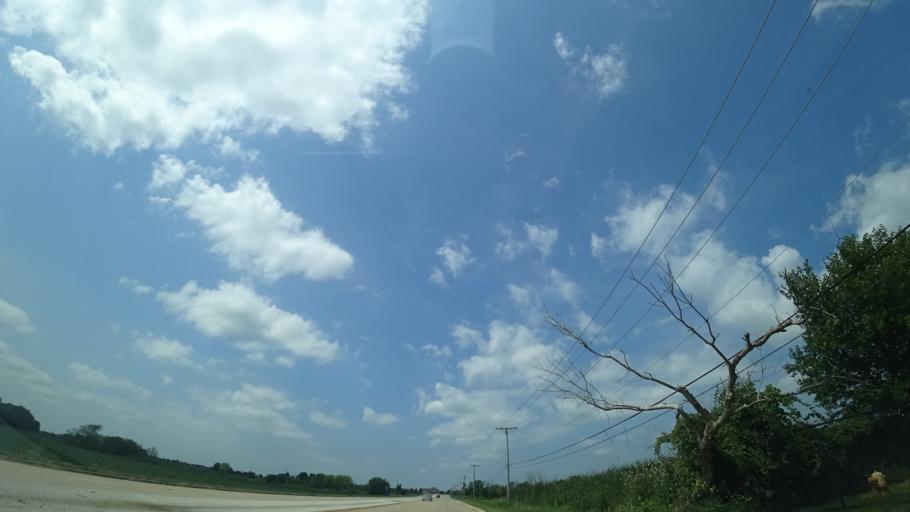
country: US
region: Illinois
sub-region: Will County
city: Frankfort Square
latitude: 41.5273
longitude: -87.7809
